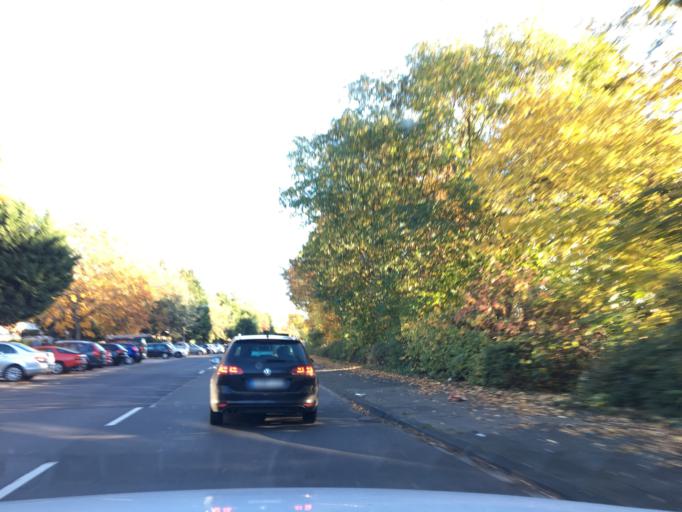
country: DE
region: North Rhine-Westphalia
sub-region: Regierungsbezirk Koln
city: Bilderstoeckchen
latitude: 50.9714
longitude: 6.9248
